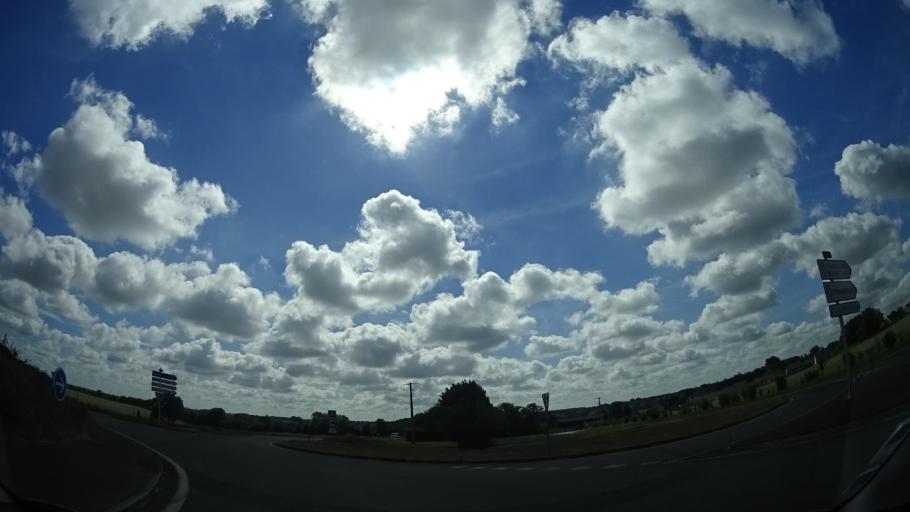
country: FR
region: Pays de la Loire
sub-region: Departement de la Mayenne
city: Entrammes
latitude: 48.0146
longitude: -0.6715
